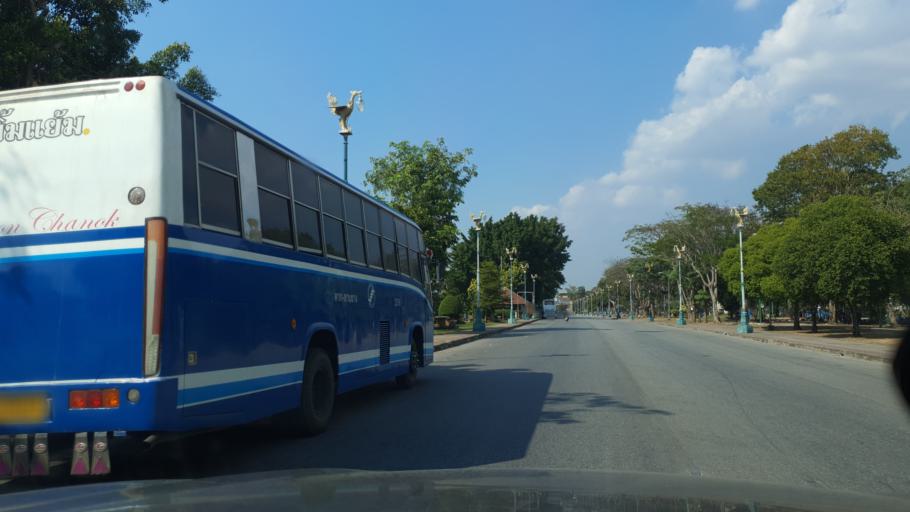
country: TH
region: Tak
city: Tak
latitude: 16.8802
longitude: 99.1199
